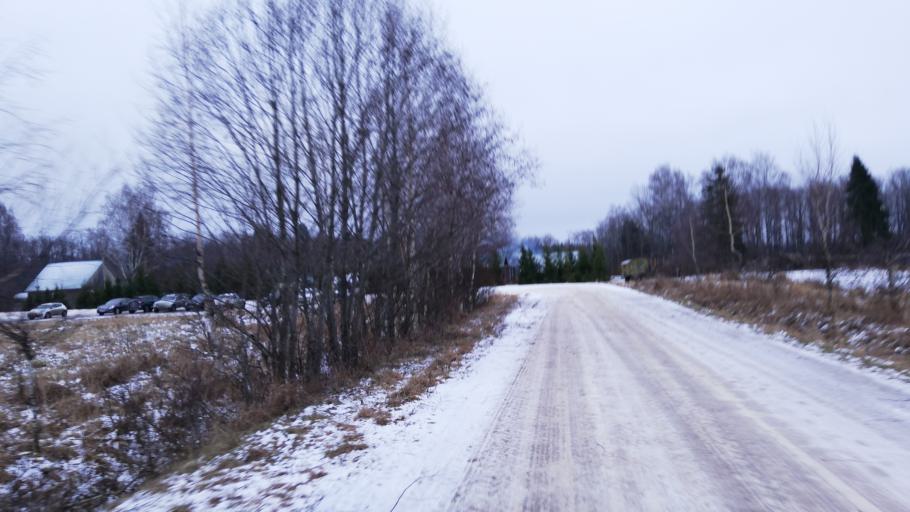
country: RU
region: Kostroma
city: Krasnoye-na-Volge
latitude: 57.6740
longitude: 41.2049
